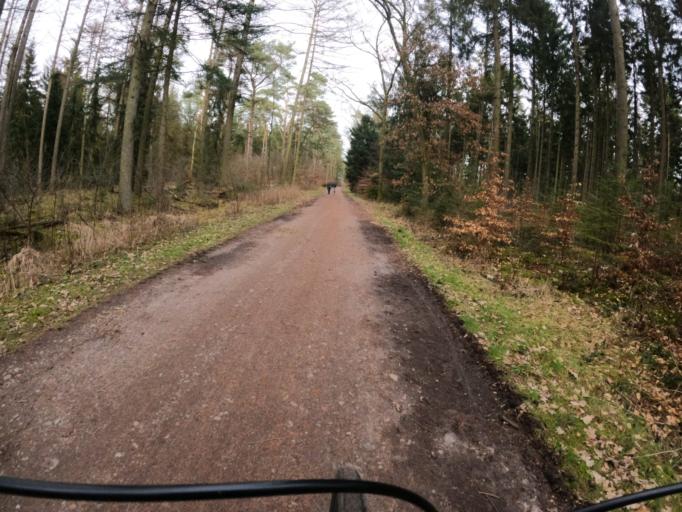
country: DE
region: Schleswig-Holstein
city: Appen
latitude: 53.6130
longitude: 9.7474
